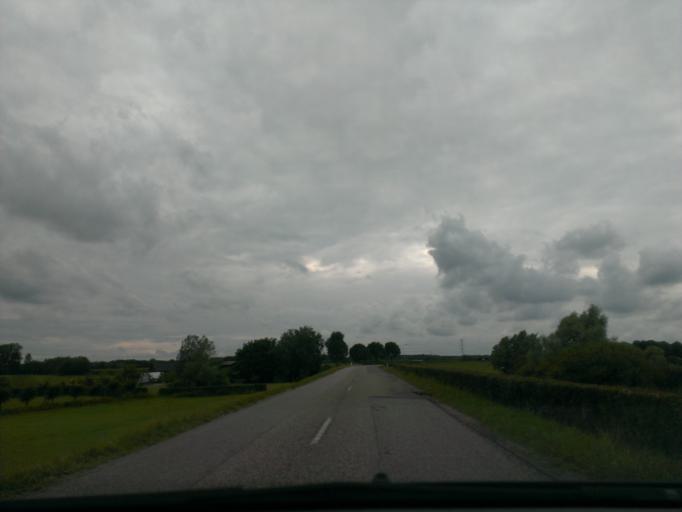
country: NL
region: Gelderland
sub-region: Gemeente Epe
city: Oene
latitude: 52.3588
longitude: 6.0772
